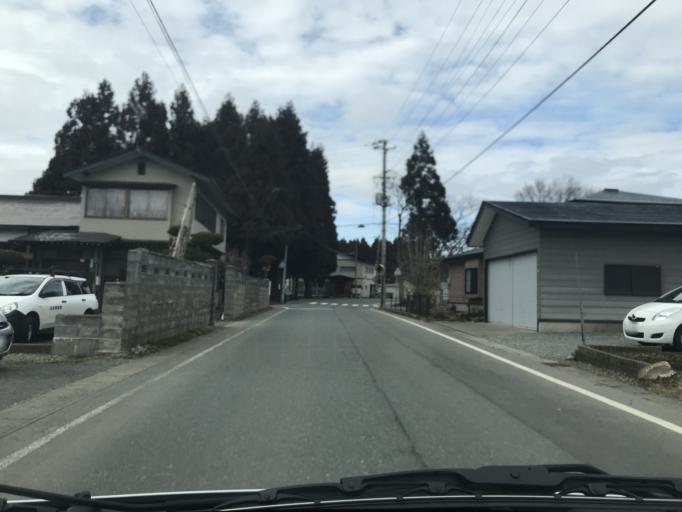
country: JP
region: Iwate
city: Kitakami
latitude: 39.3107
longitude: 140.9884
